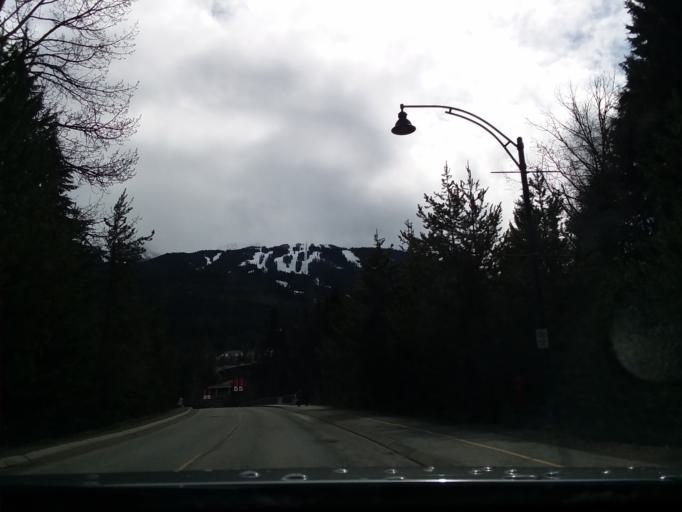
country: CA
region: British Columbia
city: Whistler
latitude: 50.1198
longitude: -122.9499
